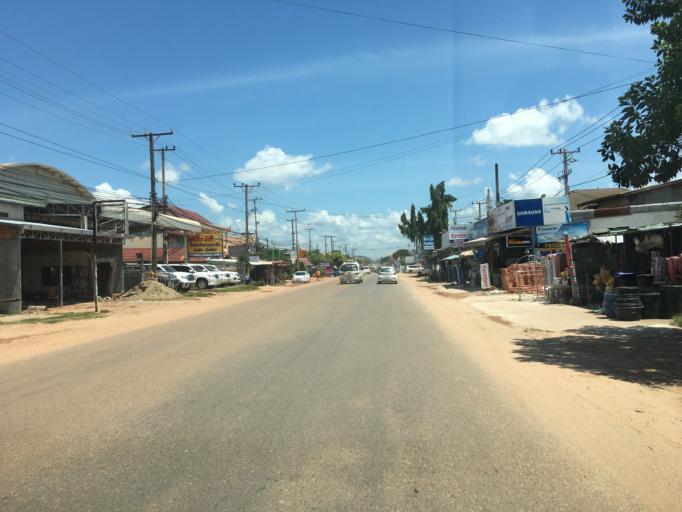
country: TH
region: Nong Khai
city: Si Chiang Mai
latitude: 18.0037
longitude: 102.5445
